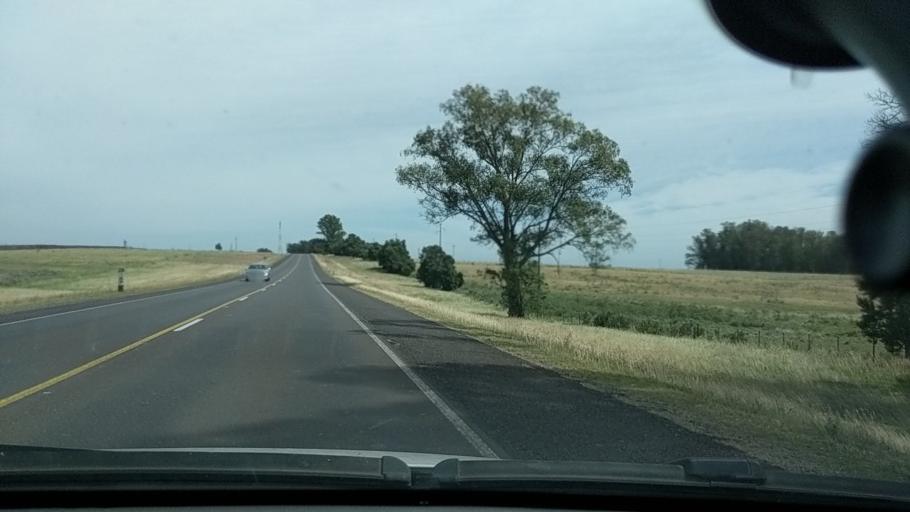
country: UY
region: Durazno
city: Durazno
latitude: -33.5066
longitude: -56.4177
